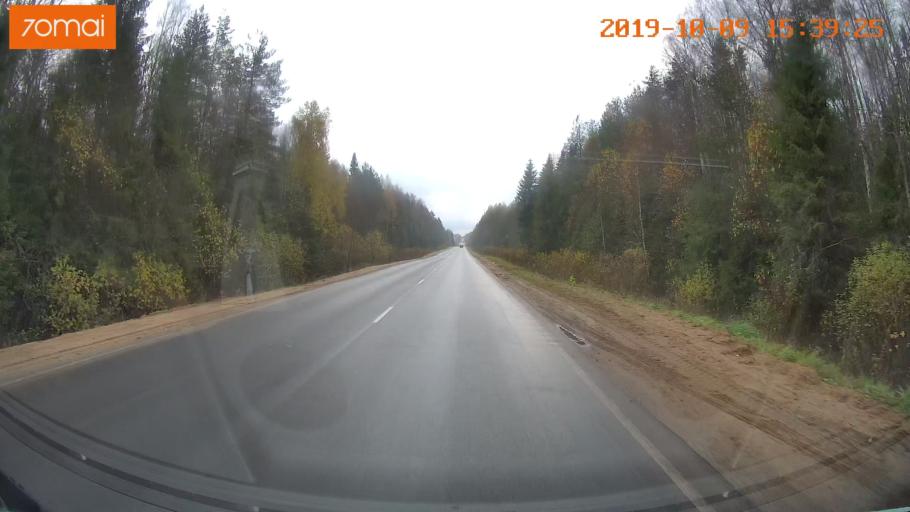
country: RU
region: Kostroma
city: Oktyabr'skiy
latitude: 57.8973
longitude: 41.1649
